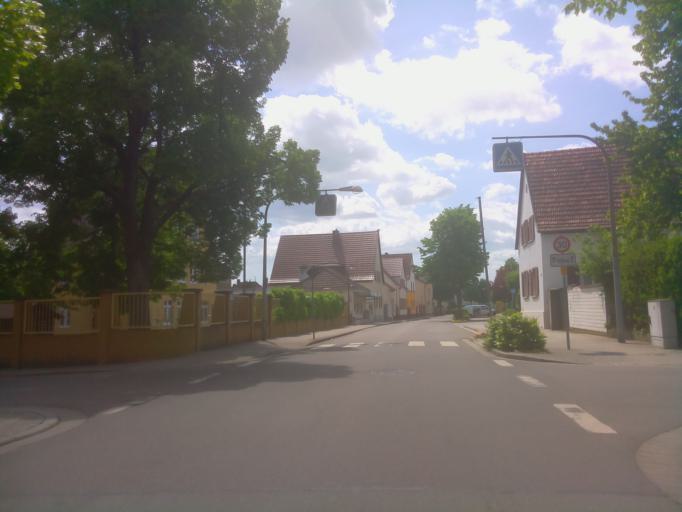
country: DE
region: Rheinland-Pfalz
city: Otterstadt
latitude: 49.3732
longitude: 8.4516
